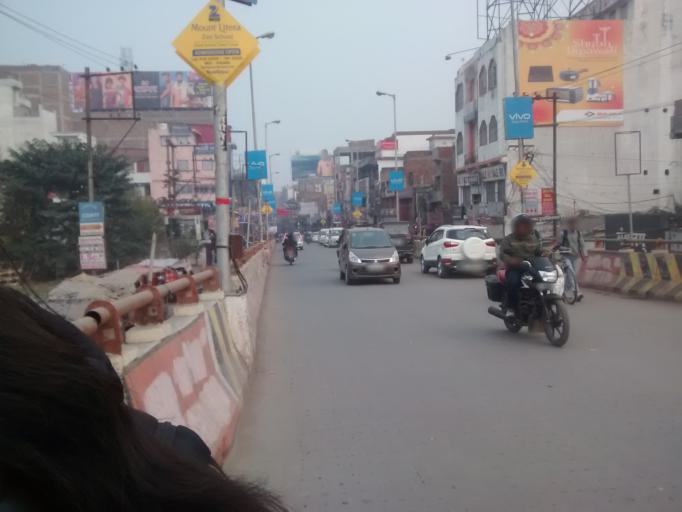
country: IN
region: Bihar
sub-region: Muzaffarpur
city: Muzaffarpur
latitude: 26.1196
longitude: 85.3874
